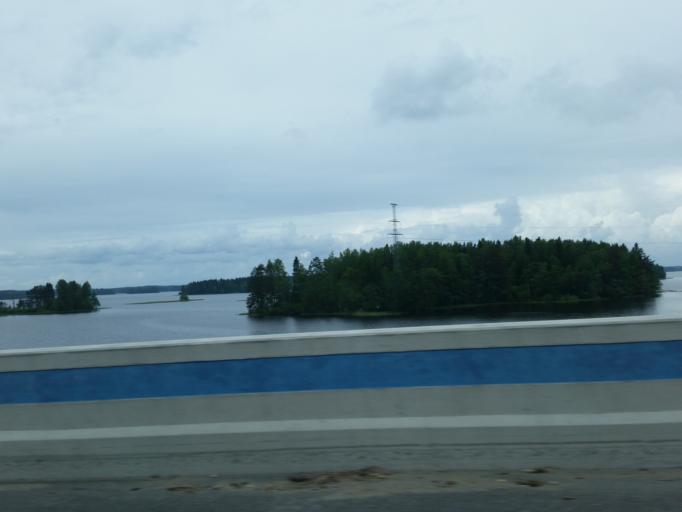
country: FI
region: Northern Savo
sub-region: Kuopio
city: Kuopio
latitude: 62.9458
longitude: 27.6701
